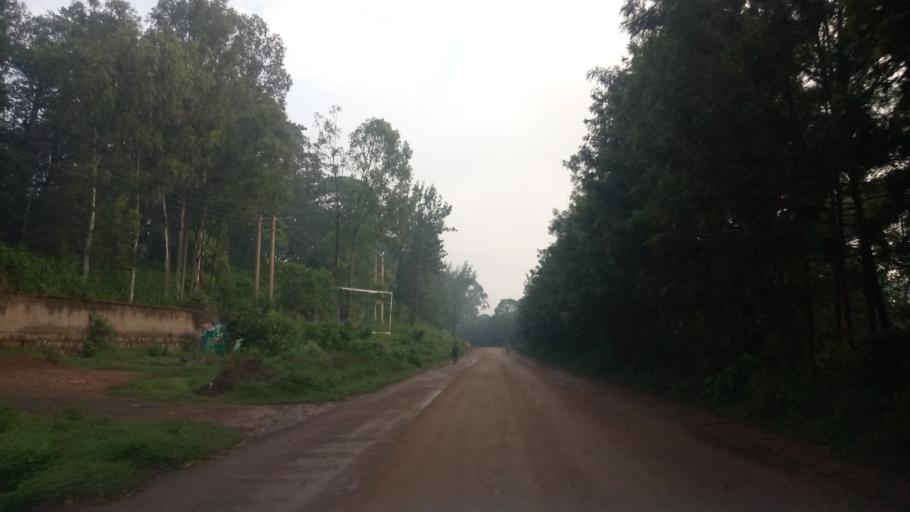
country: ET
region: Oromiya
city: Jima
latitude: 7.6831
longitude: 36.8333
